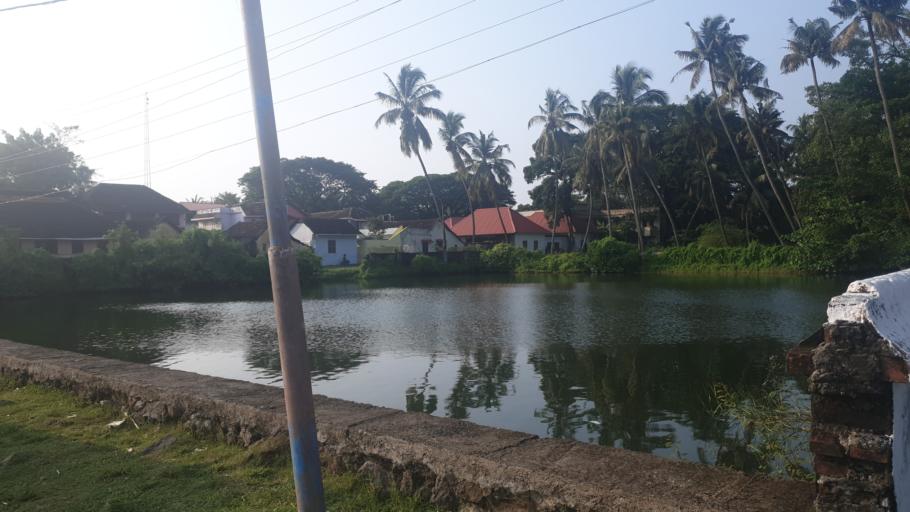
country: IN
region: Kerala
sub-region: Ernakulam
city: Cochin
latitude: 9.9579
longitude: 76.2590
